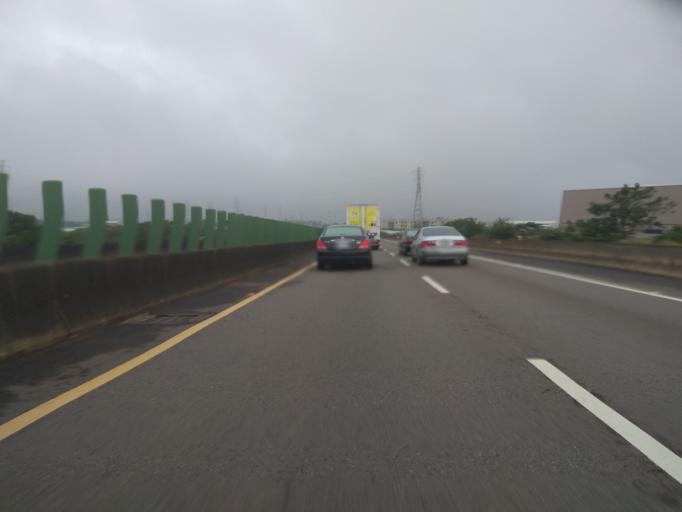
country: TW
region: Taiwan
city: Taoyuan City
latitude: 24.9737
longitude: 121.1342
